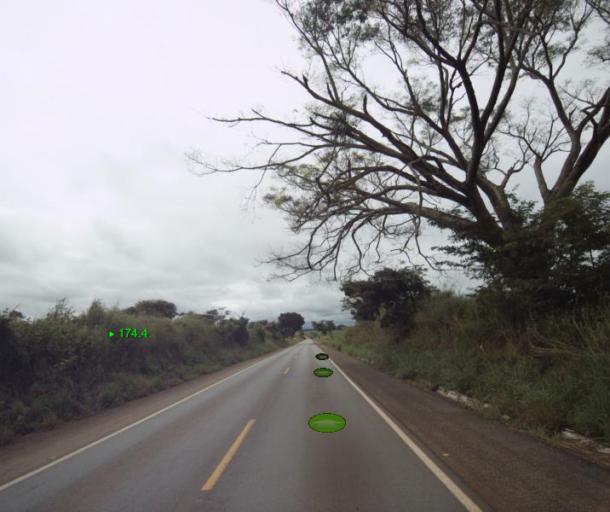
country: BR
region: Goias
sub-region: Uruacu
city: Uruacu
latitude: -14.6798
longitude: -49.1332
